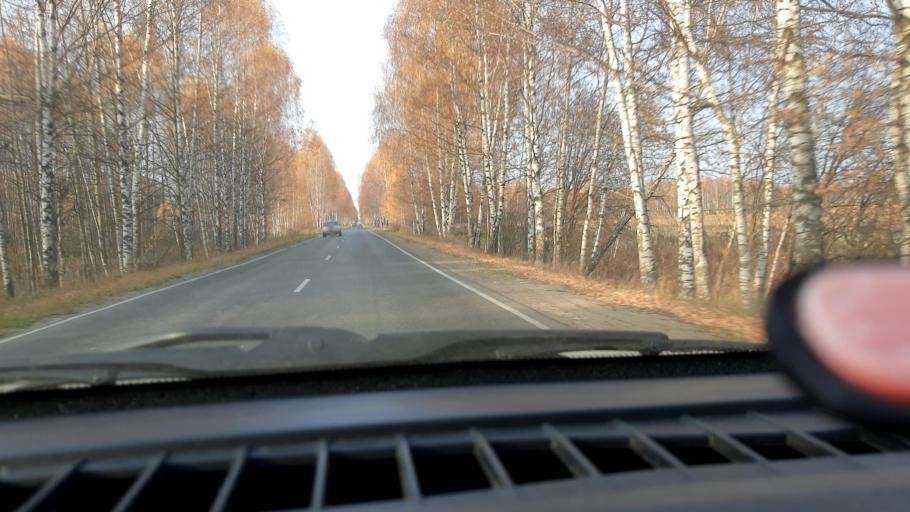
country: RU
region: Nizjnij Novgorod
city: Neklyudovo
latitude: 56.4815
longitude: 43.8699
